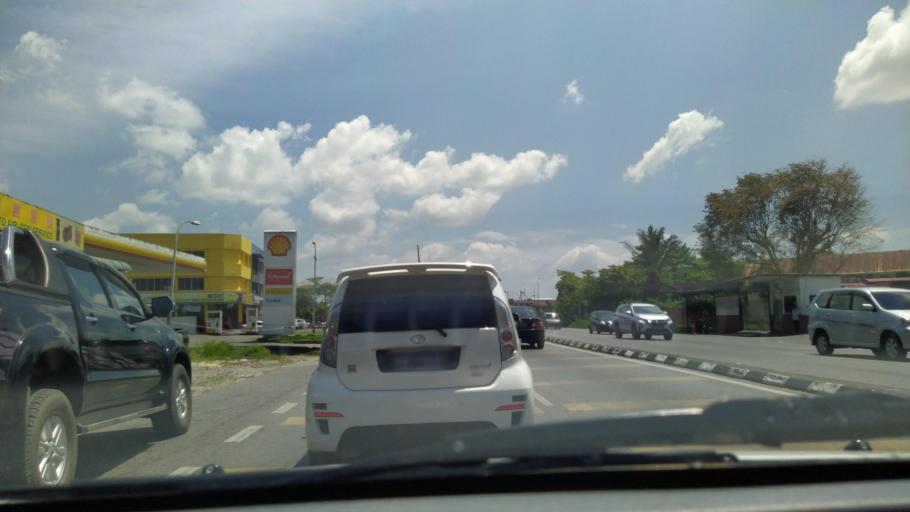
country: MY
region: Sarawak
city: Sibu
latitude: 2.2958
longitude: 111.8415
